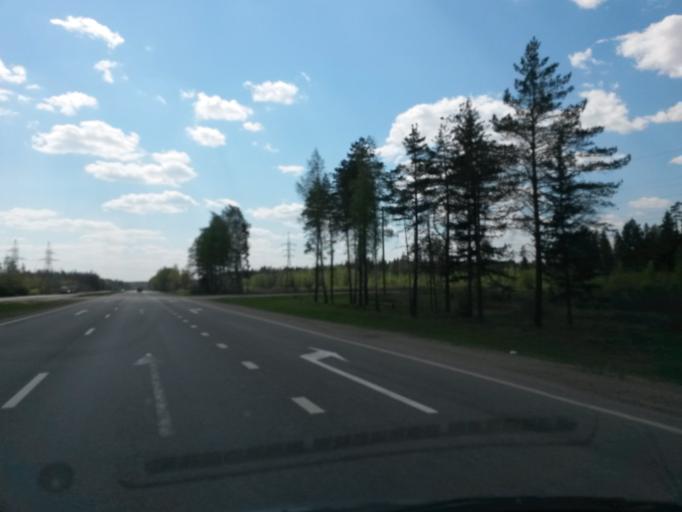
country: RU
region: Jaroslavl
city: Krasnyye Tkachi
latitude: 57.4810
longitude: 39.7704
